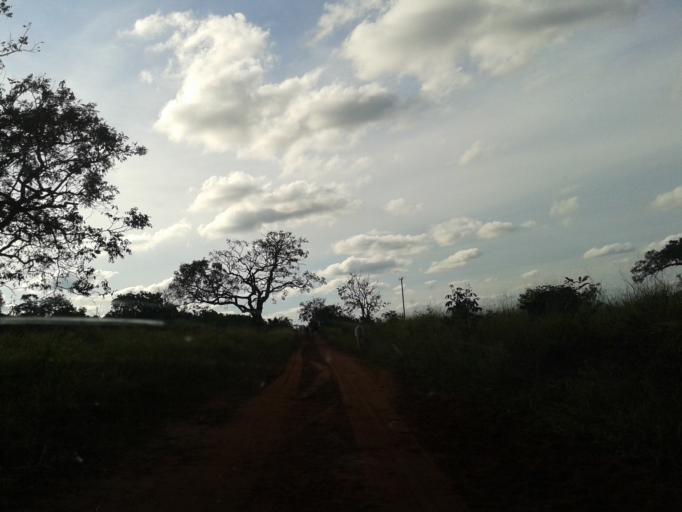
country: BR
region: Minas Gerais
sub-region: Campina Verde
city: Campina Verde
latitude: -19.4118
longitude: -49.7453
